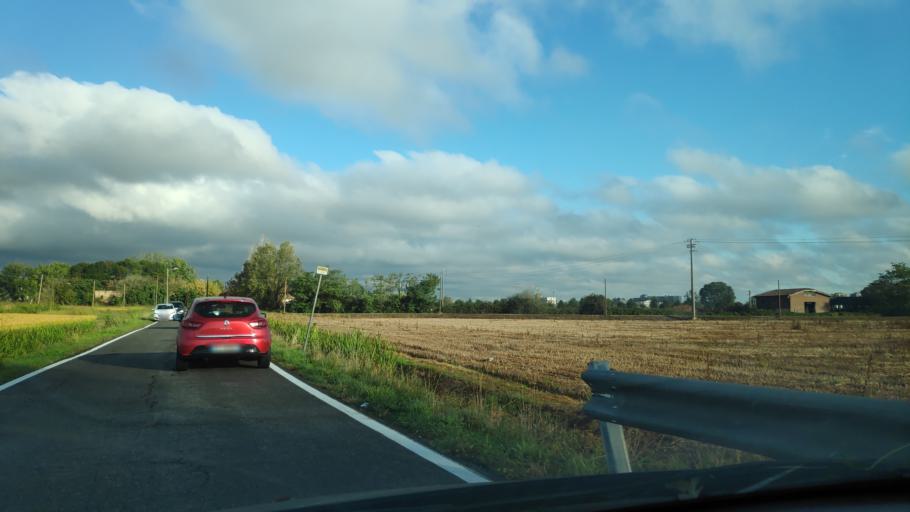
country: IT
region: Lombardy
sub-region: Citta metropolitana di Milano
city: Opera
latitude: 45.3841
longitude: 9.2051
